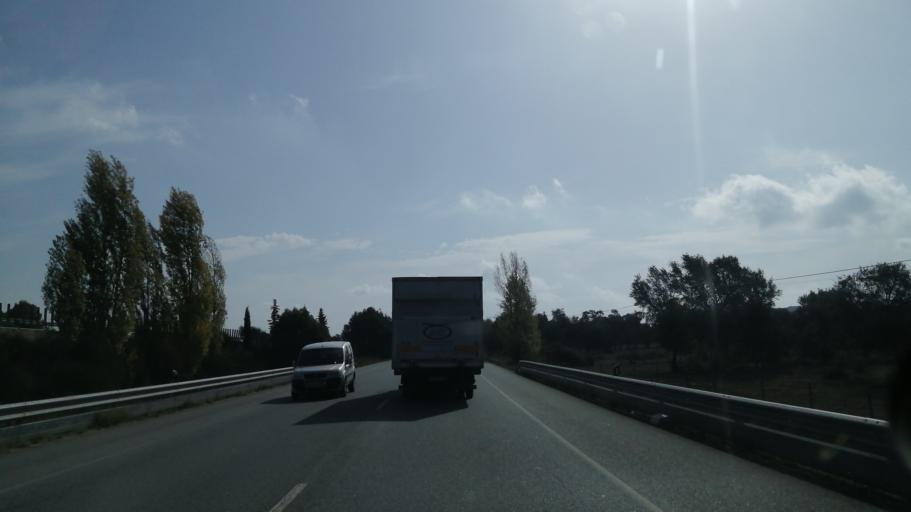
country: PT
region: Evora
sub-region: Montemor-O-Novo
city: Montemor-o-Novo
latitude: 38.6378
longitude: -8.1292
